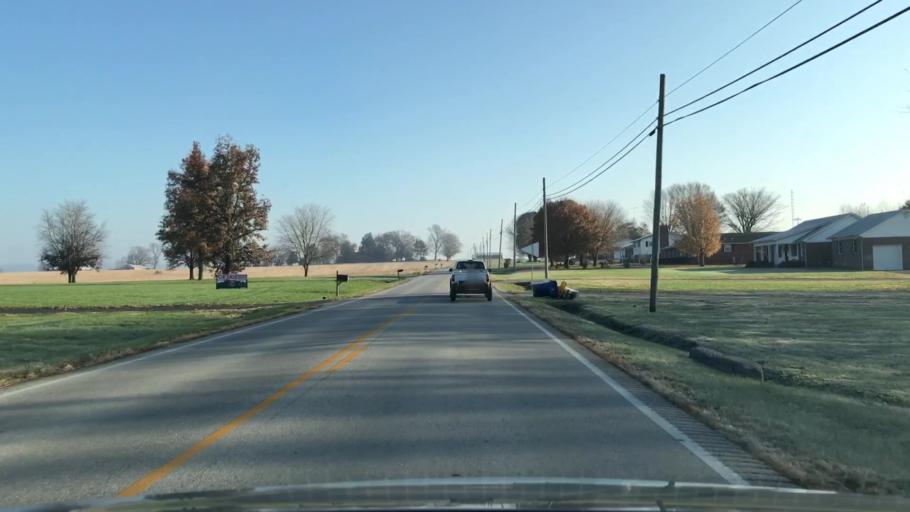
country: US
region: Kentucky
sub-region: Edmonson County
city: Brownsville
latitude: 37.0561
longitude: -86.3010
